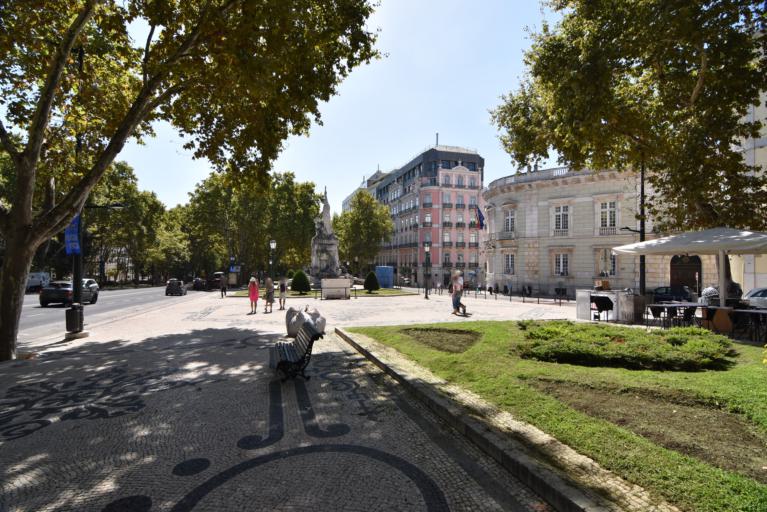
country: PT
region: Lisbon
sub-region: Lisbon
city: Lisbon
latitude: 38.7199
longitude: -9.1454
